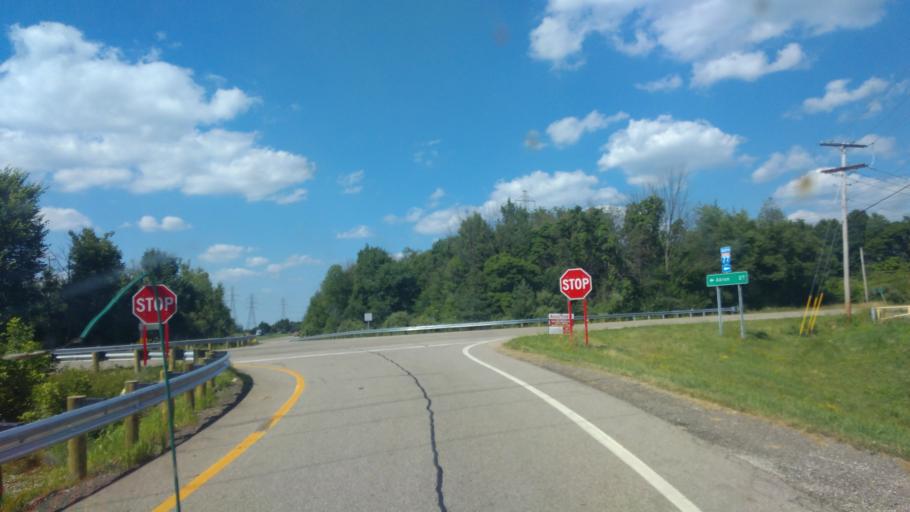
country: US
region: Ohio
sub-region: Stark County
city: Richville
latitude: 40.7288
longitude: -81.4180
